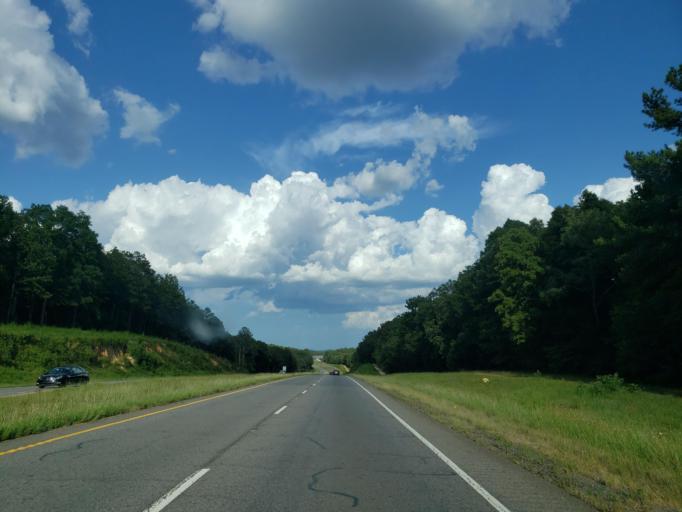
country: US
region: Georgia
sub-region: Bartow County
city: Euharlee
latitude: 34.2031
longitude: -85.0122
